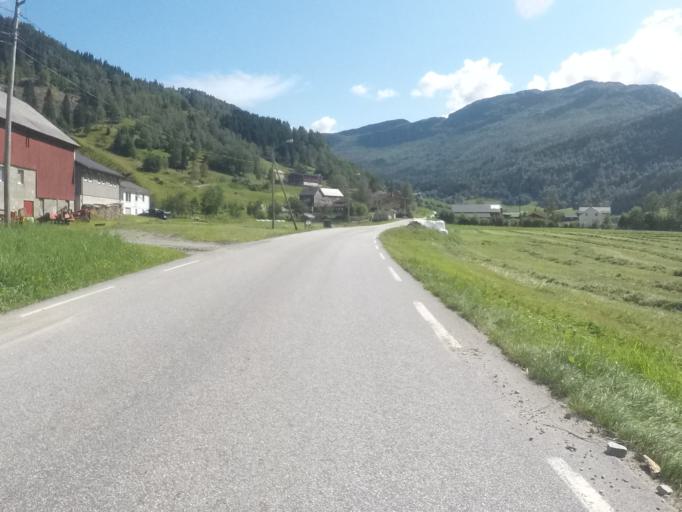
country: NO
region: Sogn og Fjordane
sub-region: Hoyanger
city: Hoyanger
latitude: 61.4206
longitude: 6.1541
